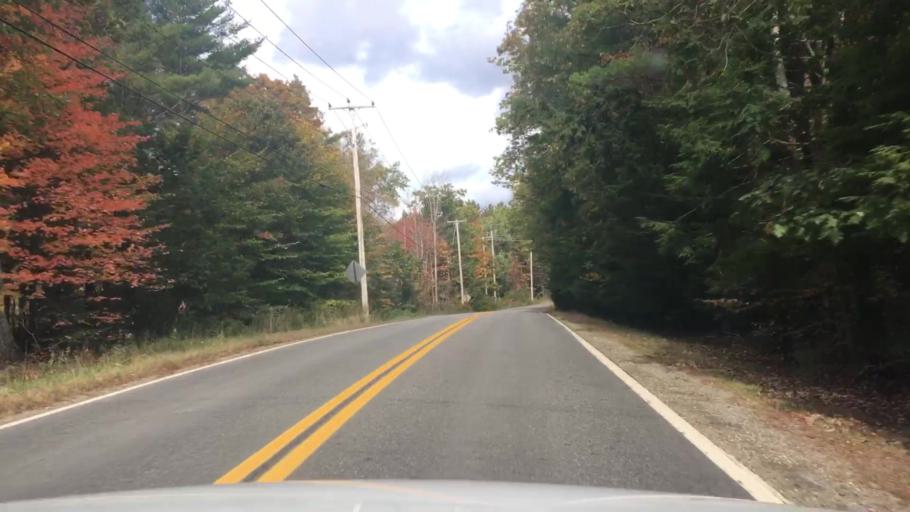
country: US
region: Maine
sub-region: Knox County
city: Hope
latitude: 44.3045
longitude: -69.1142
